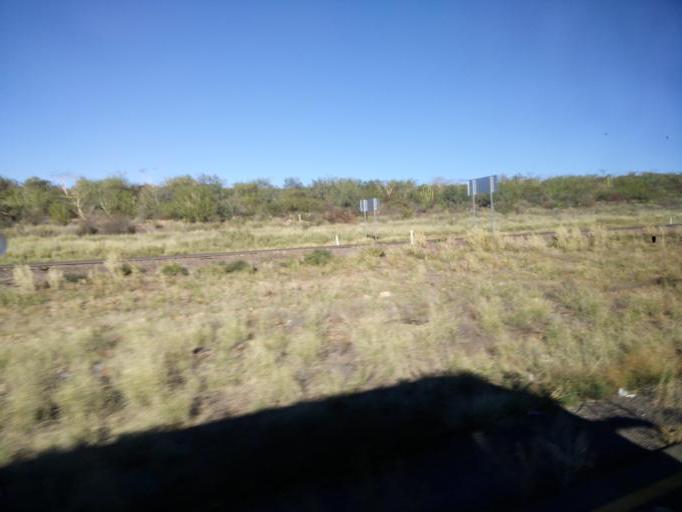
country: MX
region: Sonora
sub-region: Empalme
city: La Palma
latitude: 28.4370
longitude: -111.0456
